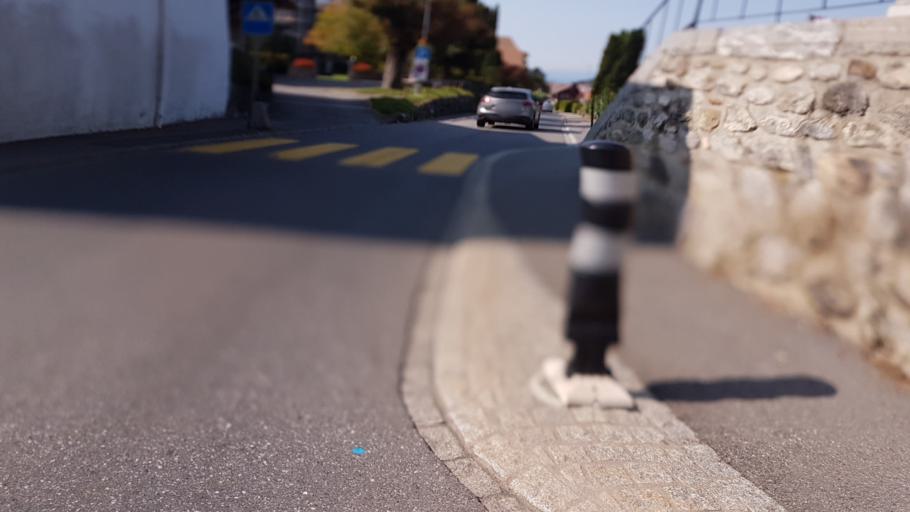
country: CH
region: Bern
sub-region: Frutigen-Niedersimmental District
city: Aeschi
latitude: 46.6596
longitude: 7.6954
